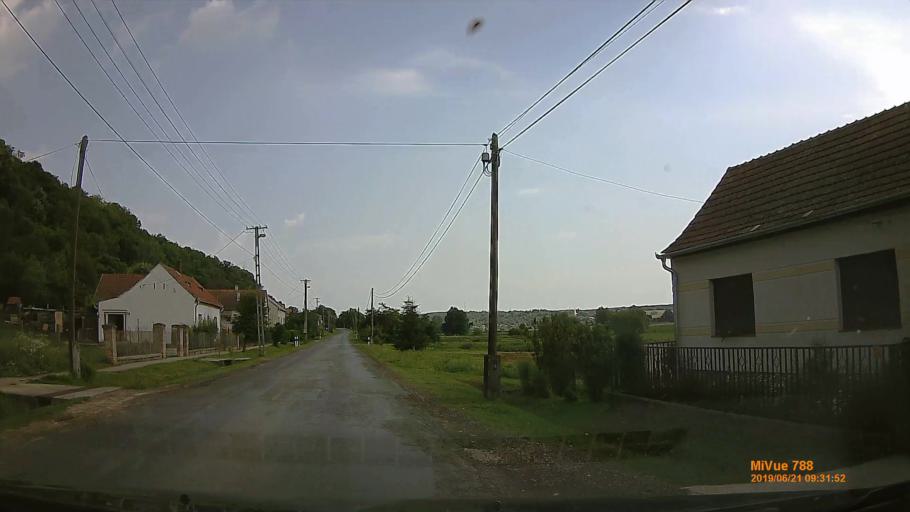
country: HU
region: Somogy
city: Taszar
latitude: 46.3080
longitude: 17.8821
